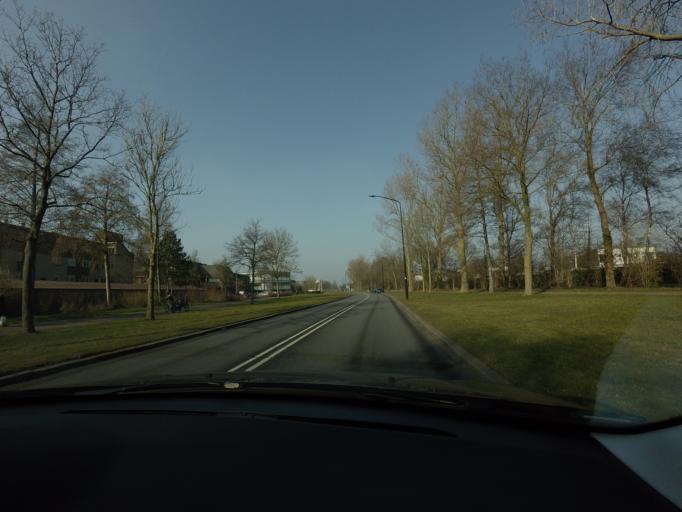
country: NL
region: North Holland
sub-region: Gemeente Heerhugowaard
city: Heerhugowaard
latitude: 52.6601
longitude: 4.8365
